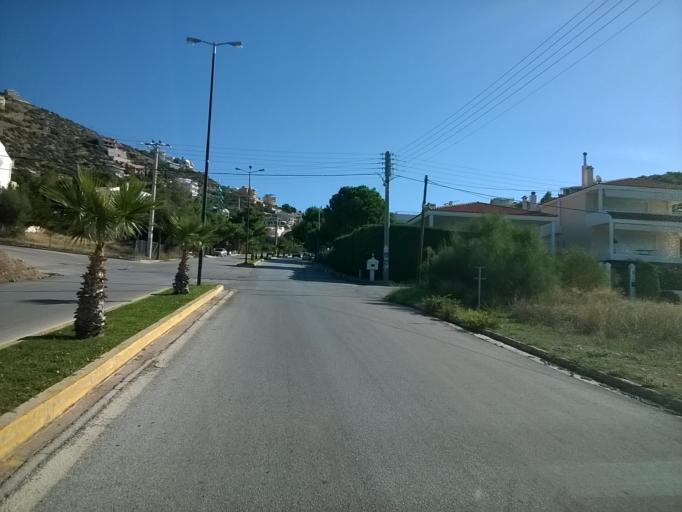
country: GR
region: Attica
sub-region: Nomarchia Anatolikis Attikis
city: Saronida
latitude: 37.7465
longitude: 23.9174
